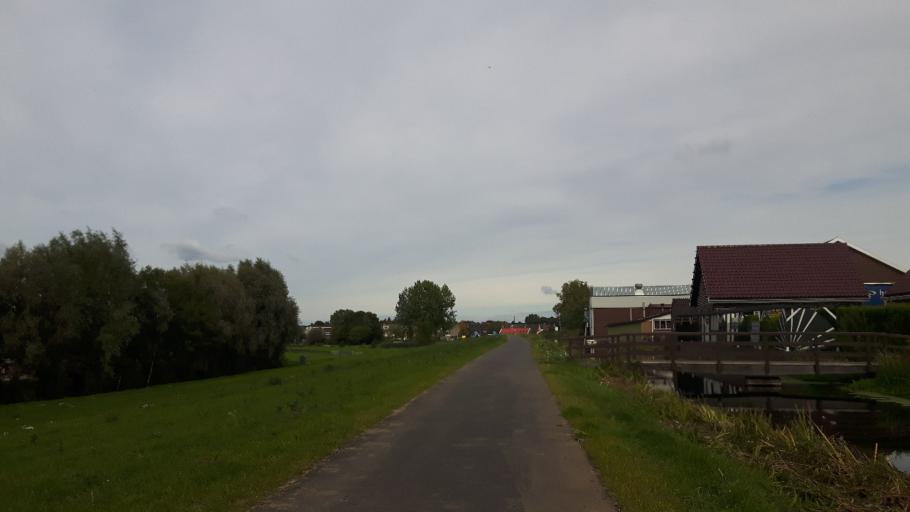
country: NL
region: South Holland
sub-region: Gemeente Nieuwkoop
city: Nieuwkoop
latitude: 52.1385
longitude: 4.7670
